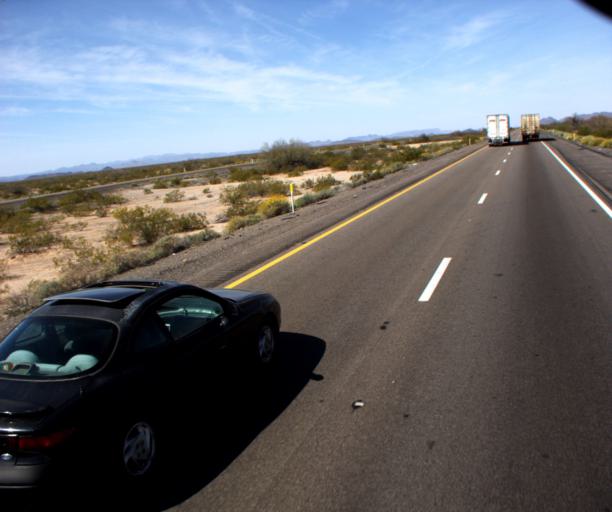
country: US
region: Arizona
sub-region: La Paz County
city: Salome
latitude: 33.5871
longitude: -113.4711
